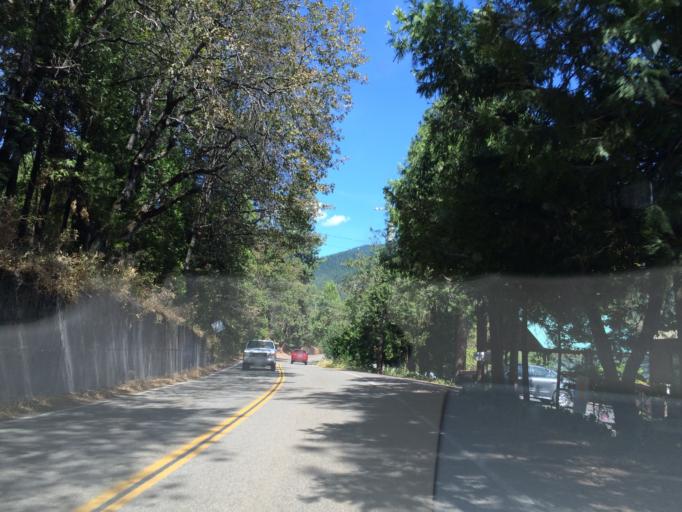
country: US
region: California
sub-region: Siskiyou County
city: Dunsmuir
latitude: 41.1998
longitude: -122.2773
